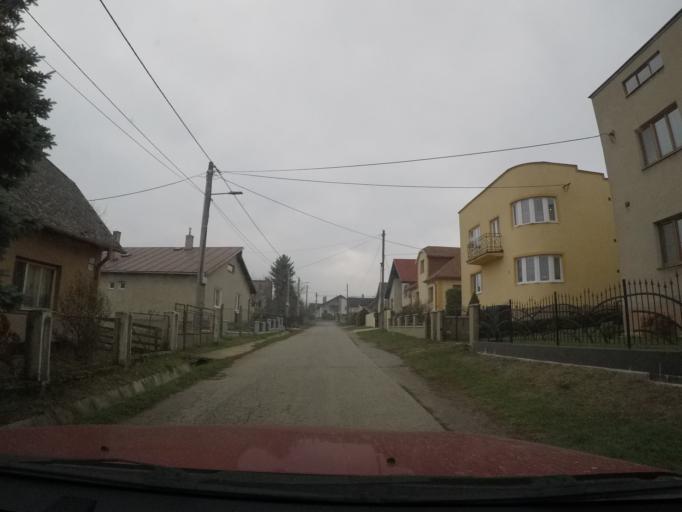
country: SK
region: Presovsky
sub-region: Okres Presov
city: Presov
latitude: 48.8780
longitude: 21.2713
